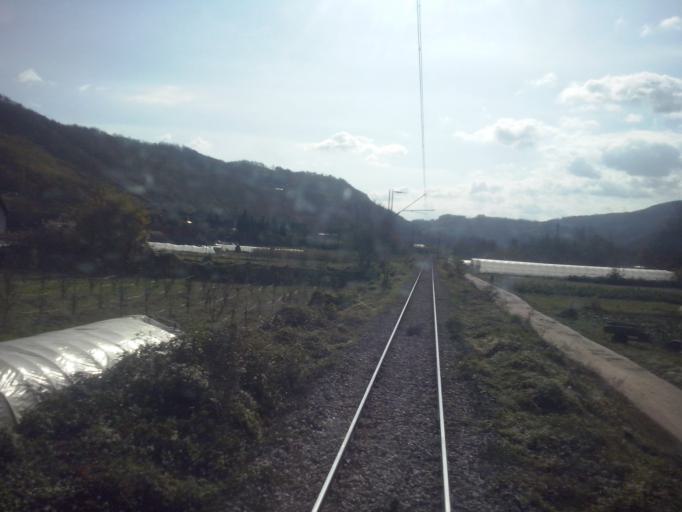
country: RS
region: Central Serbia
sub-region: Zlatiborski Okrug
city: Pozega
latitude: 43.9362
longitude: 19.9876
